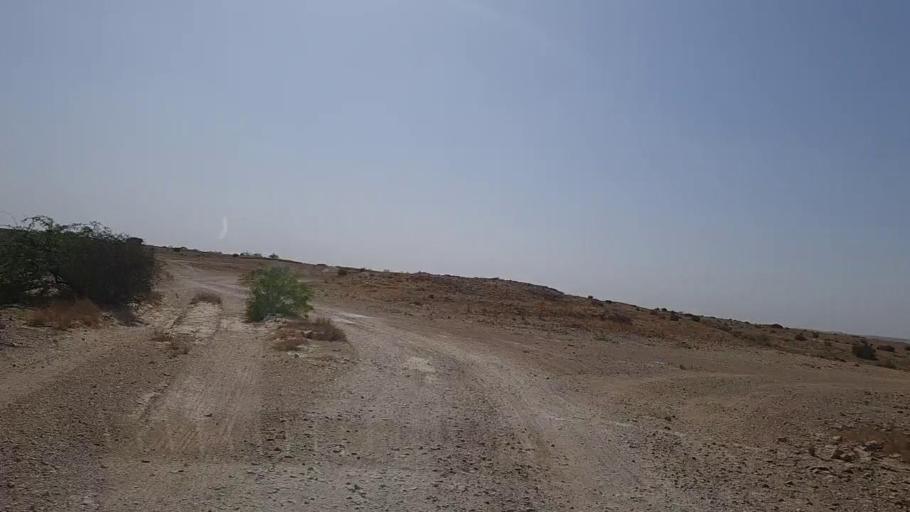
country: PK
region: Sindh
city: Kotri
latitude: 25.1641
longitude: 68.1803
